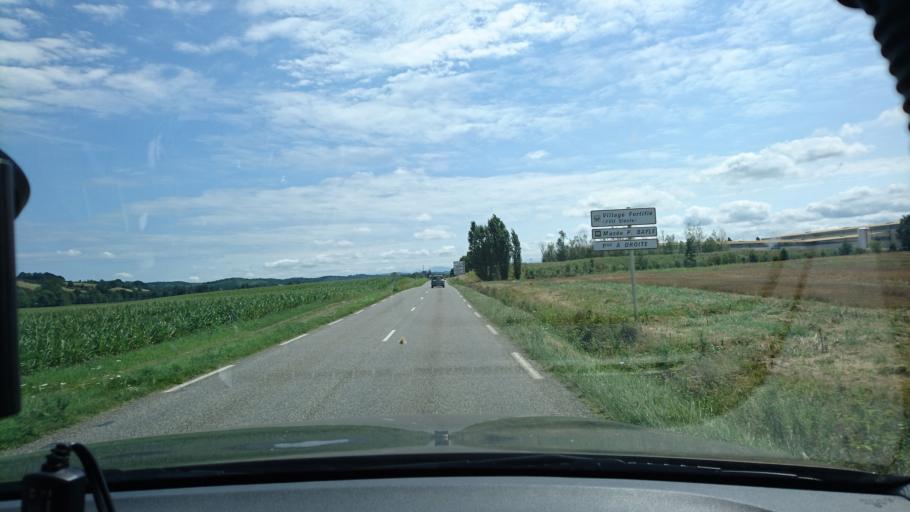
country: FR
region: Midi-Pyrenees
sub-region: Departement de la Haute-Garonne
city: Gaillac-Toulza
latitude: 43.1677
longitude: 1.4141
